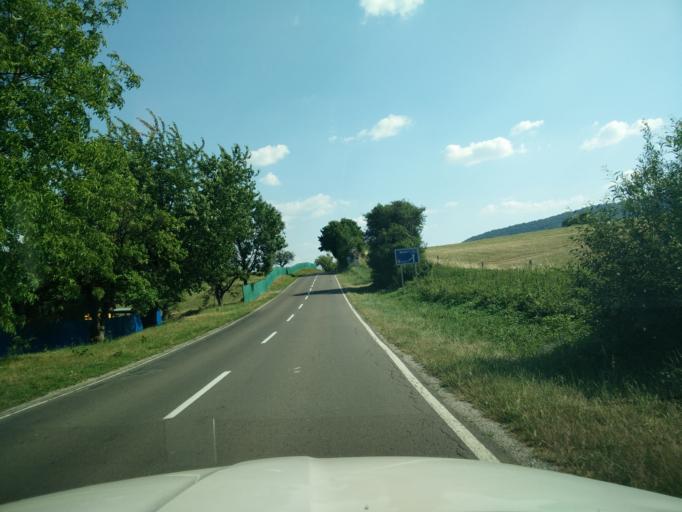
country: SK
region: Nitriansky
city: Novaky
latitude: 48.8036
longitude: 18.4759
